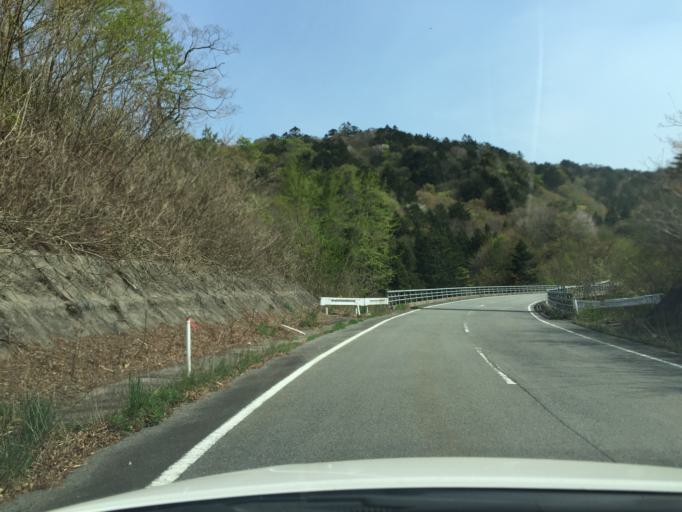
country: JP
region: Fukushima
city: Iwaki
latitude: 37.2555
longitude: 140.8505
